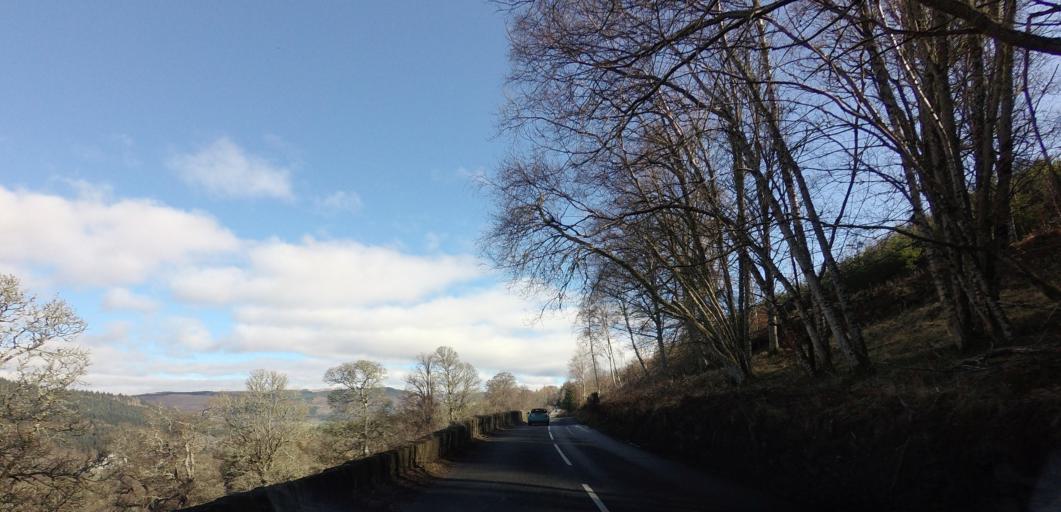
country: GB
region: Scotland
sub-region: Perth and Kinross
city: Aberfeldy
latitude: 56.5863
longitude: -3.9796
